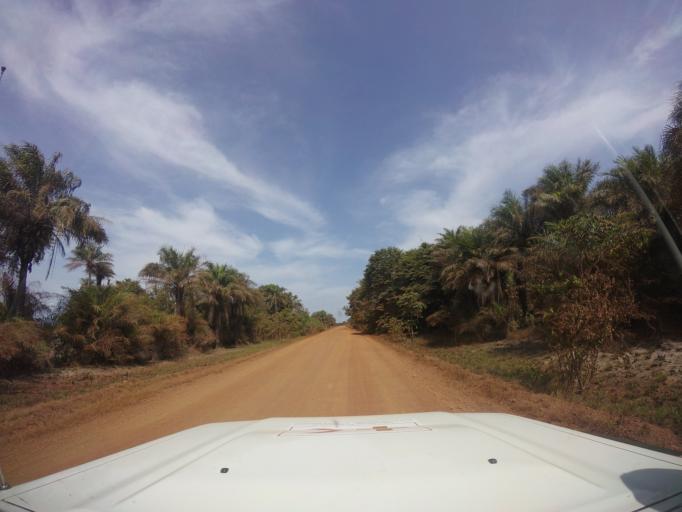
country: LR
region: Grand Cape Mount
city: Robertsport
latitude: 6.6884
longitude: -11.2549
